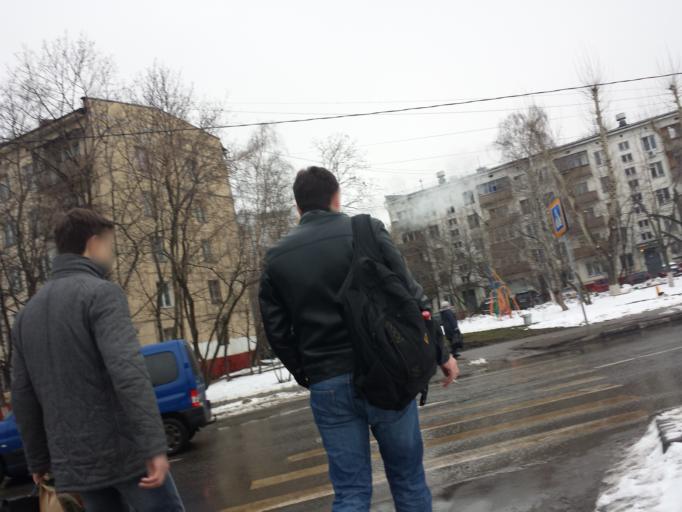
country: RU
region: Moscow
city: Novyye Kuz'minki
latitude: 55.7076
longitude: 37.7653
